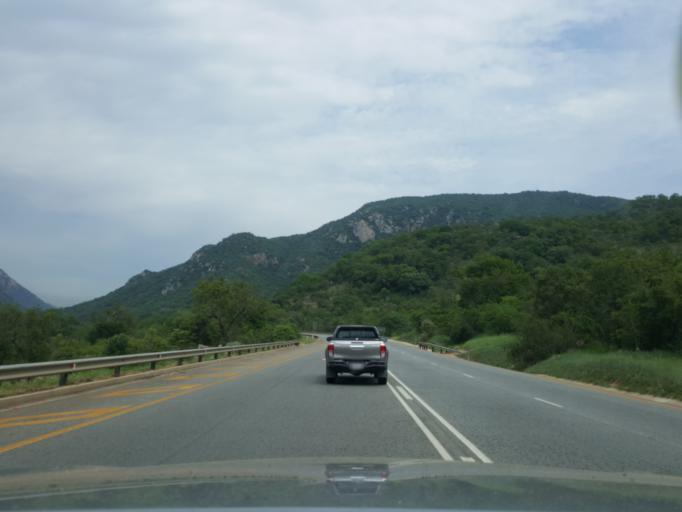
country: SZ
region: Hhohho
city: Ntfonjeni
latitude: -25.5310
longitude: 31.2856
